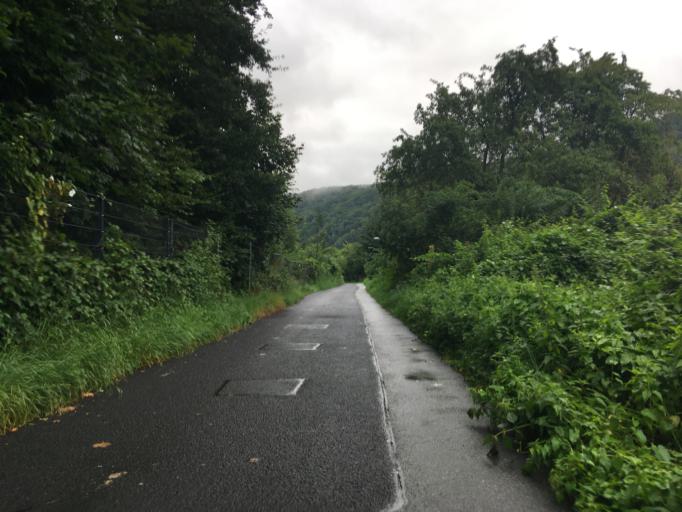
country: DE
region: Saxony
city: Struppen
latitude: 50.9468
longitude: 14.0025
